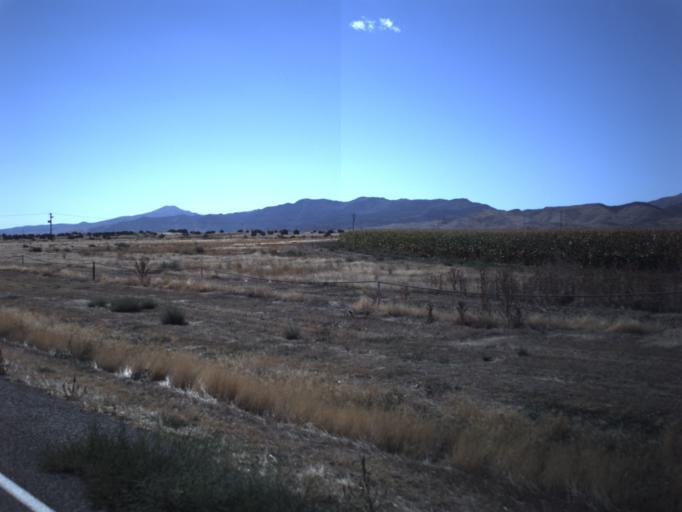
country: US
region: Utah
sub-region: Utah County
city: Genola
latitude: 40.0045
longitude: -111.9580
